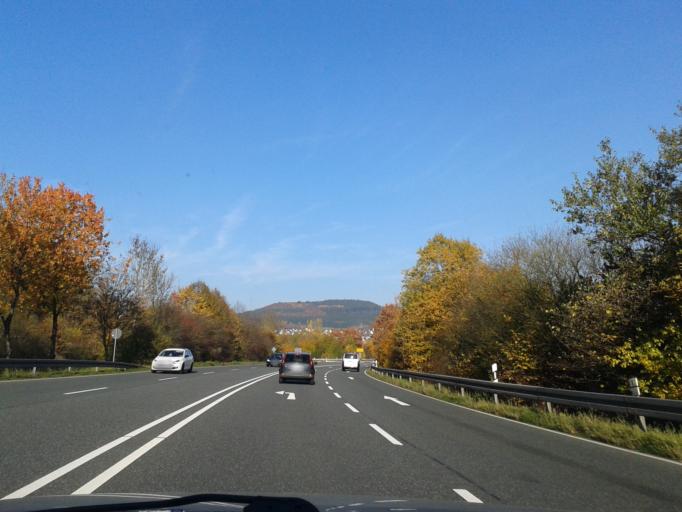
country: DE
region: Hesse
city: Dillenburg
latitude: 50.8049
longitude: 8.3370
